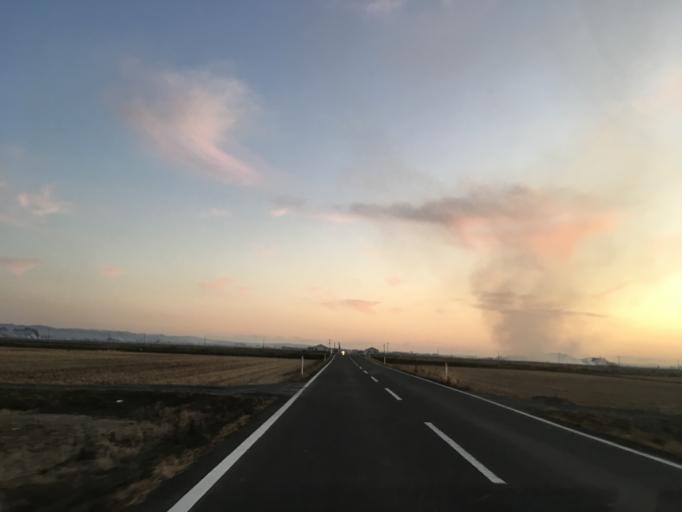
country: JP
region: Iwate
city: Ichinoseki
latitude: 38.7503
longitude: 141.2369
